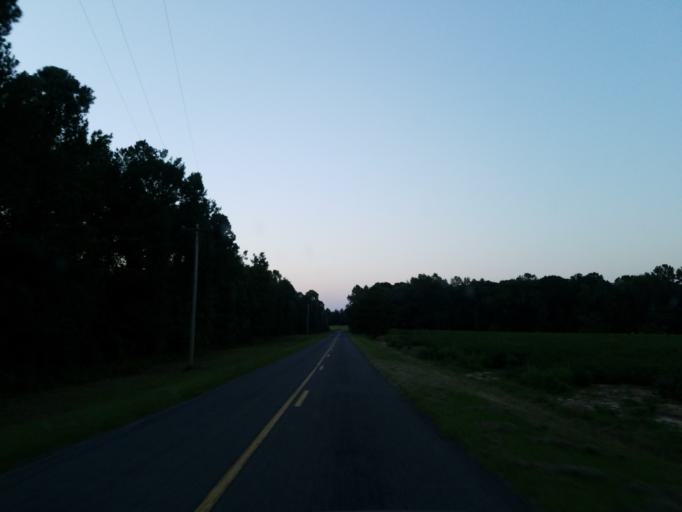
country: US
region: Georgia
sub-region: Dooly County
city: Unadilla
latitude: 32.2294
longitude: -83.7970
